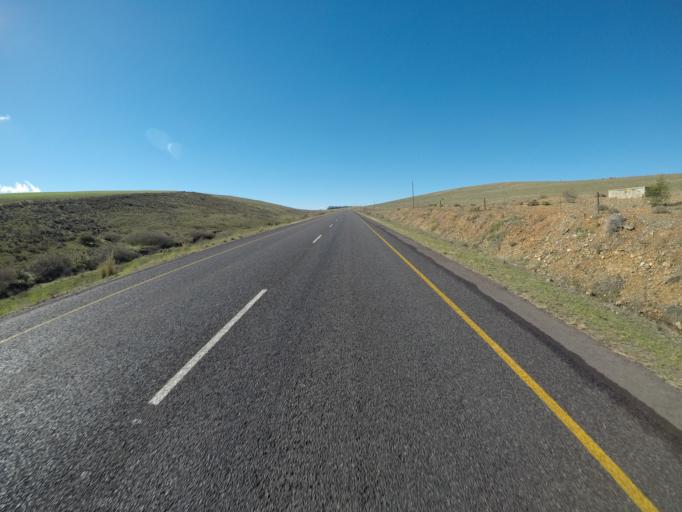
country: ZA
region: Western Cape
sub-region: Overberg District Municipality
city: Caledon
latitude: -34.1473
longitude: 19.4888
